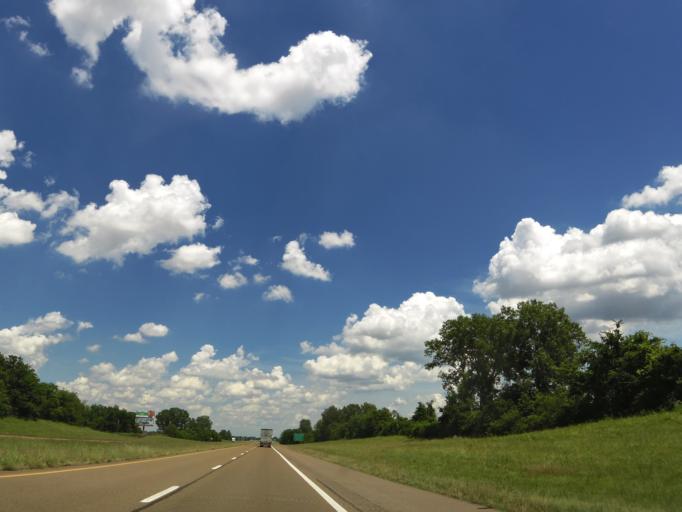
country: US
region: Tennessee
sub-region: Dyer County
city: Dyersburg
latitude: 36.0689
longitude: -89.4129
